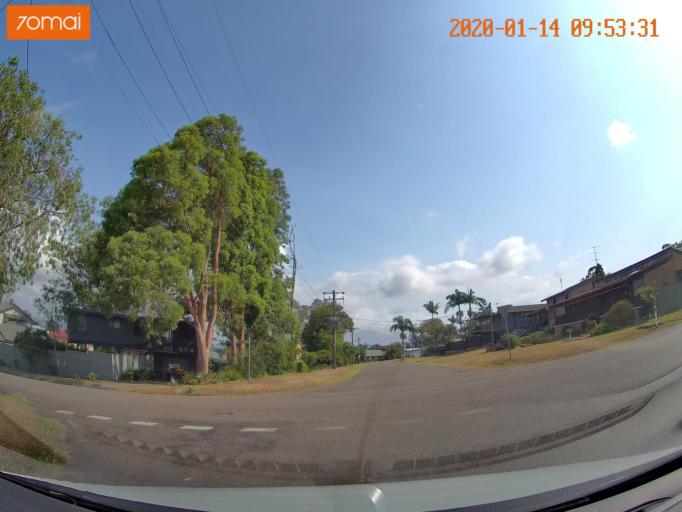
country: AU
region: New South Wales
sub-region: Lake Macquarie Shire
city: Dora Creek
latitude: -33.1082
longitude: 151.5286
